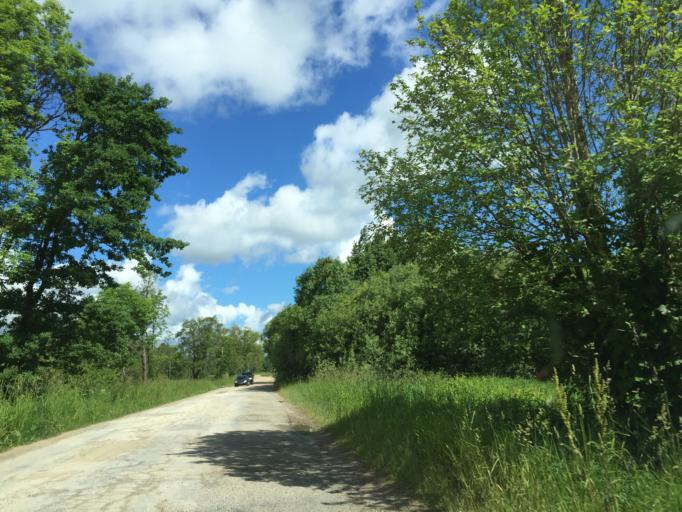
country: LV
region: Lecava
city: Iecava
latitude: 56.6122
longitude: 24.1895
